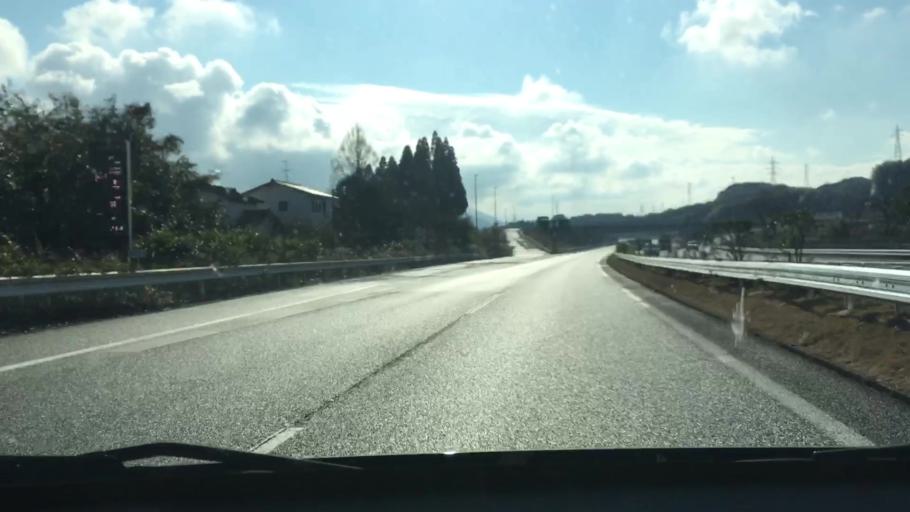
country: JP
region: Kumamoto
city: Matsubase
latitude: 32.5796
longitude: 130.7132
